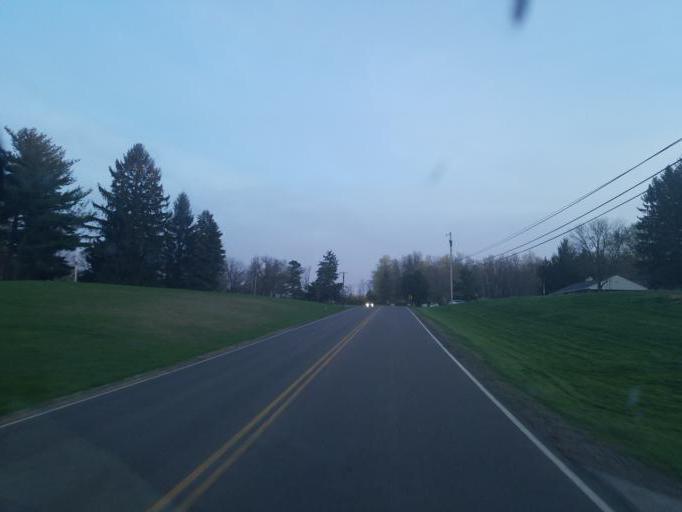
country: US
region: Ohio
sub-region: Richland County
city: Ontario
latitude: 40.7348
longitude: -82.5895
